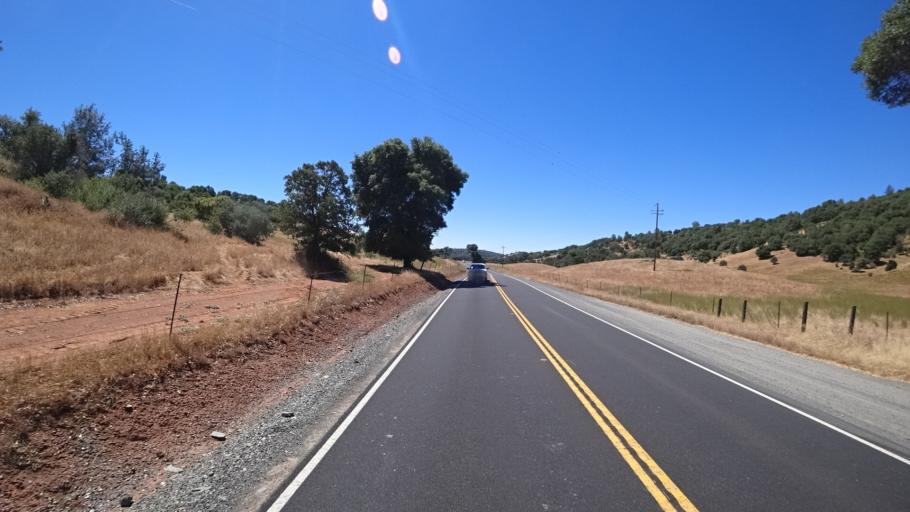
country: US
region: California
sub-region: Calaveras County
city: Copperopolis
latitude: 38.0309
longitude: -120.6479
